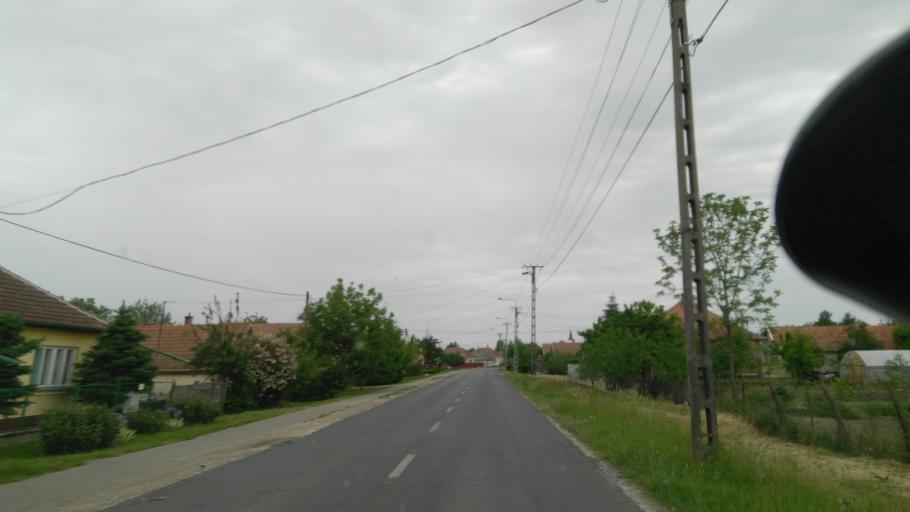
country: HU
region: Bekes
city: Doboz
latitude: 46.7337
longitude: 21.2561
